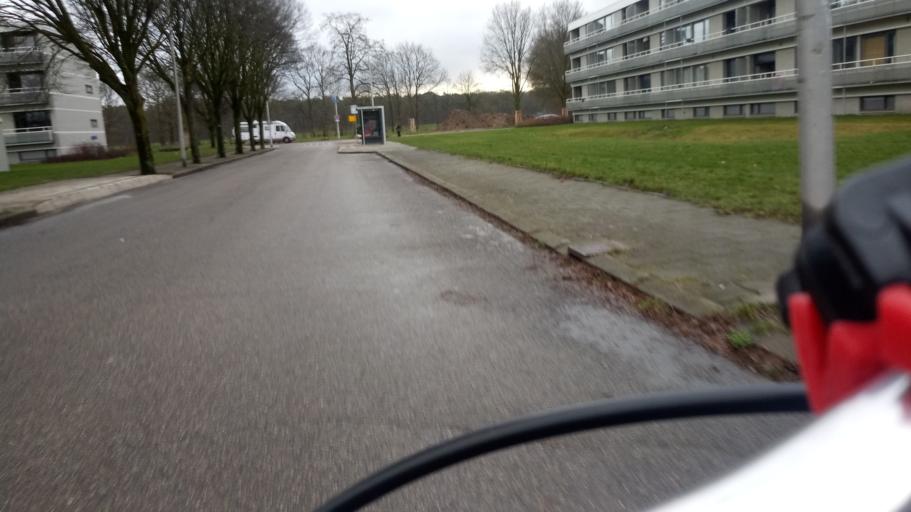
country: NL
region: Gelderland
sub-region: Gemeente Nijmegen
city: Nijmegen
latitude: 51.8062
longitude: 5.8339
